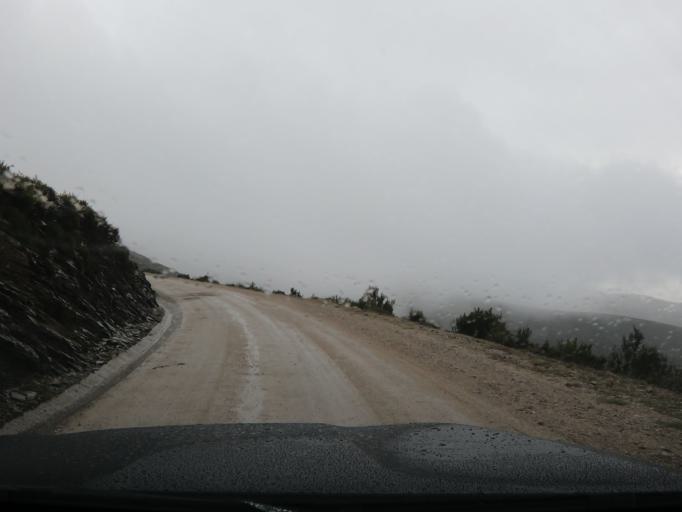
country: PT
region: Vila Real
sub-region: Vila Real
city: Vila Real
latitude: 41.3262
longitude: -7.8443
